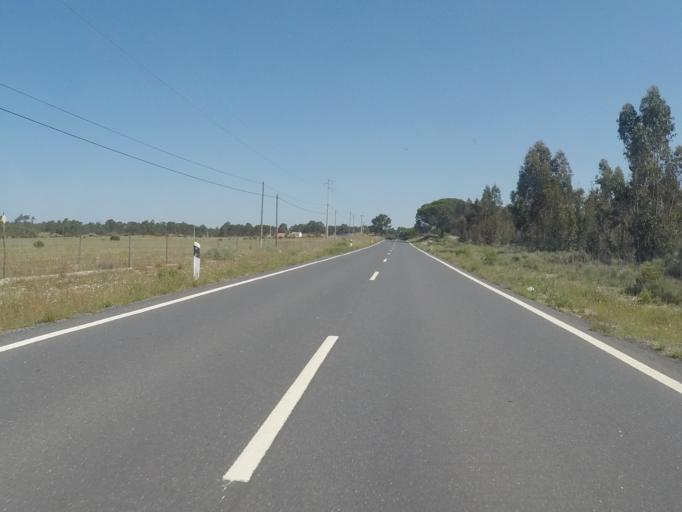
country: PT
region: Setubal
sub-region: Grandola
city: Grandola
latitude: 38.2495
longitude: -8.7375
